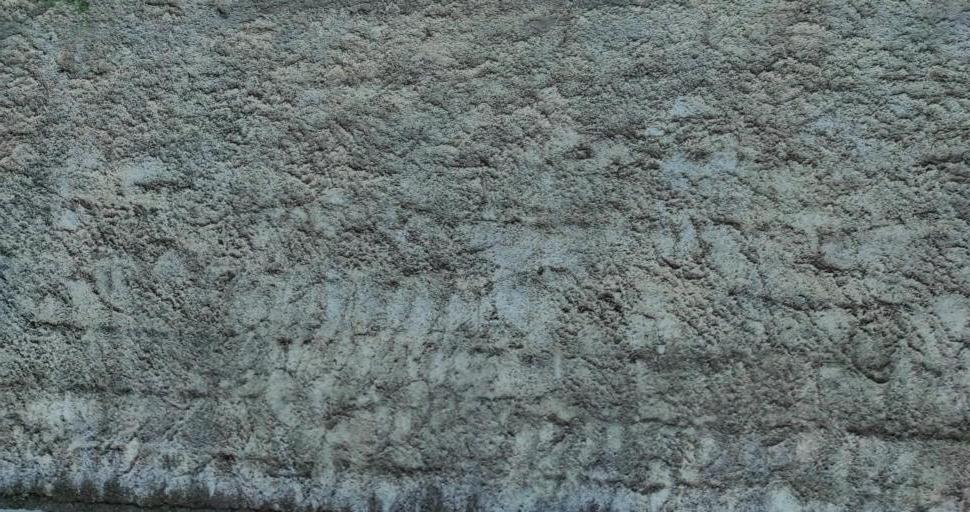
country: AL
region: Shkoder
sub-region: Rrethi i Shkodres
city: Shkoder
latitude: 42.0606
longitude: 19.5091
